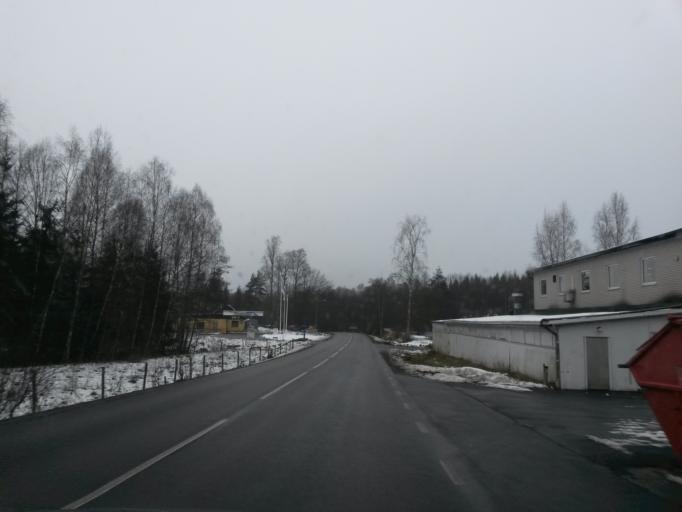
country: SE
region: Vaestra Goetaland
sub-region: Ulricehamns Kommun
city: Ulricehamn
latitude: 57.6771
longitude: 13.4001
